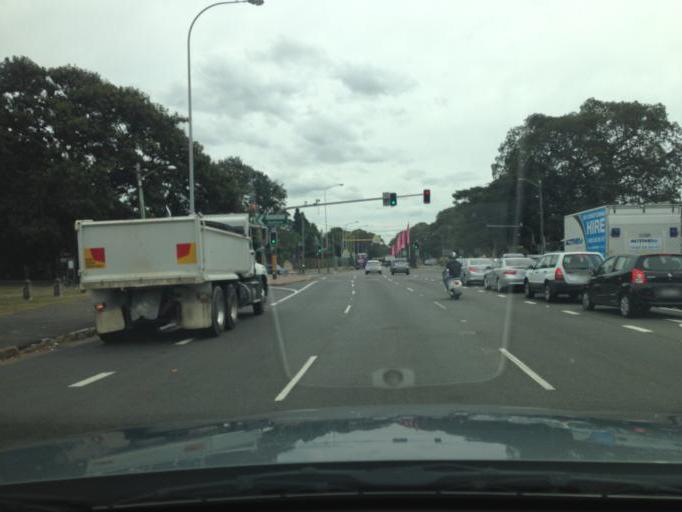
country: AU
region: New South Wales
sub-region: Woollahra
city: Paddington
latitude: -33.8959
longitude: 151.2216
